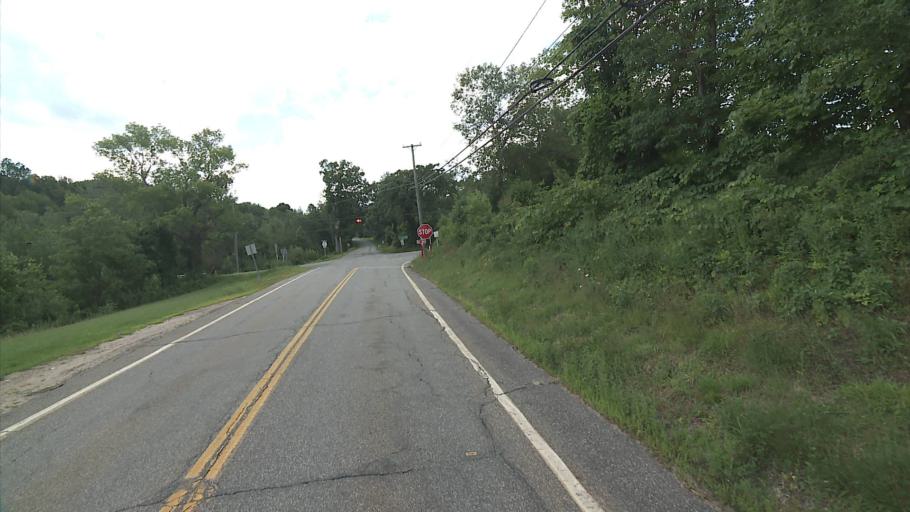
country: US
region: Connecticut
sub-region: Tolland County
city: Stafford Springs
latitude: 41.9172
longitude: -72.1911
